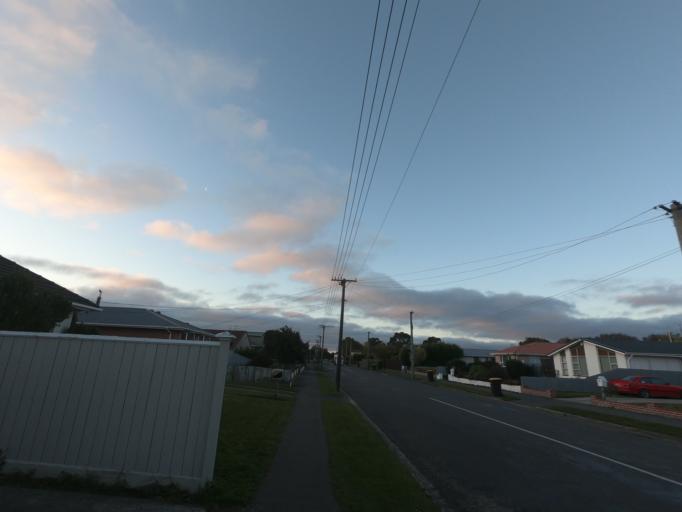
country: NZ
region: Canterbury
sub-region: Selwyn District
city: Prebbleton
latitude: -43.5731
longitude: 172.5687
